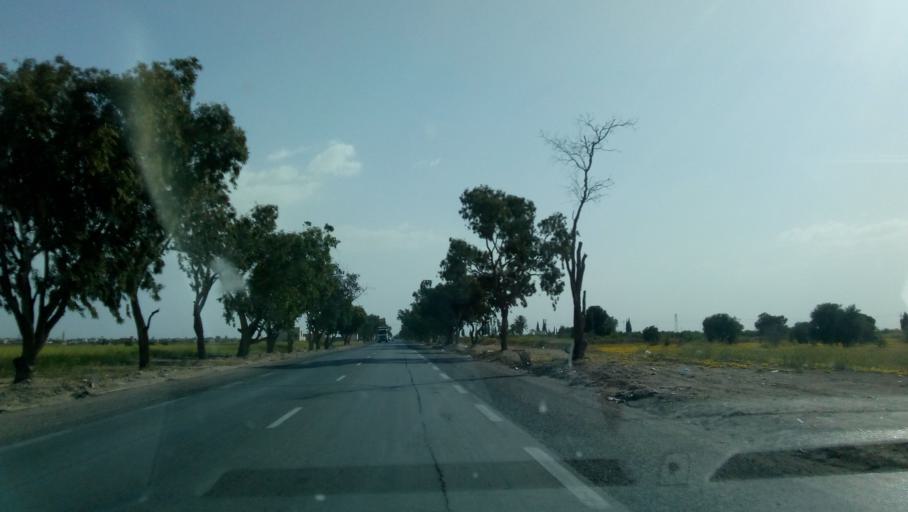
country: TN
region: Qabis
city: Gabes
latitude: 33.8927
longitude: 10.0417
